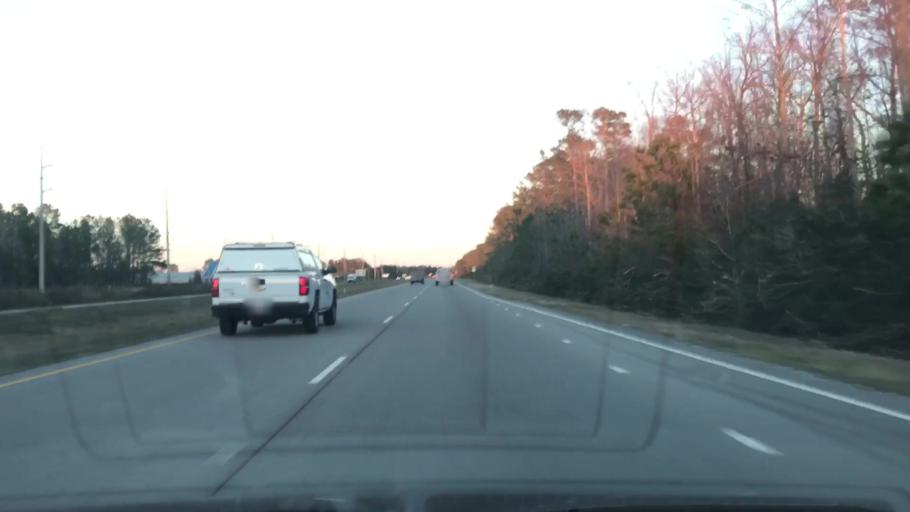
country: US
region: North Carolina
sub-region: Brunswick County
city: Shallotte
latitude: 33.9812
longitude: -78.3986
